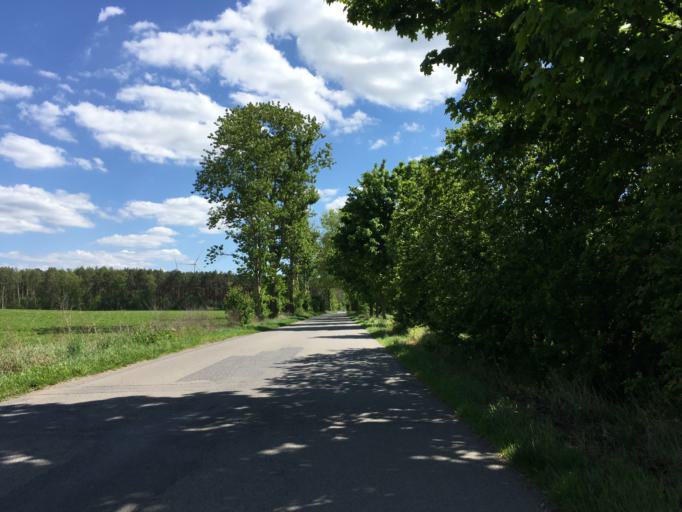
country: DE
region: Brandenburg
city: Rudnitz
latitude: 52.7012
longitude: 13.6646
